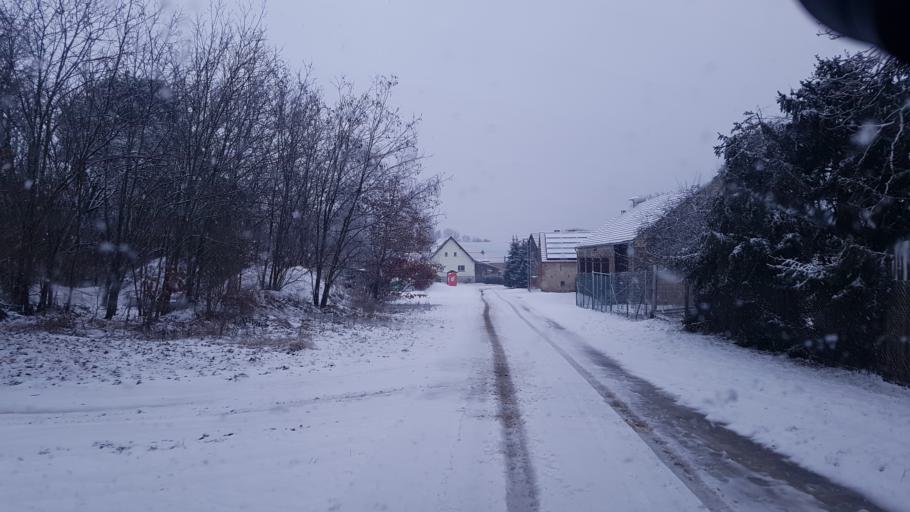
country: DE
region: Brandenburg
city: Schenkendobern
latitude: 51.9072
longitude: 14.5768
